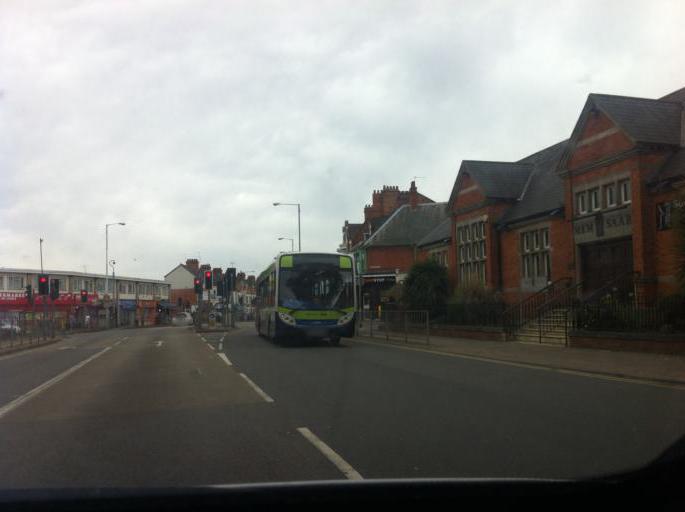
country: GB
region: England
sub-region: Northamptonshire
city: Northampton
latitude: 52.2443
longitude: -0.8716
